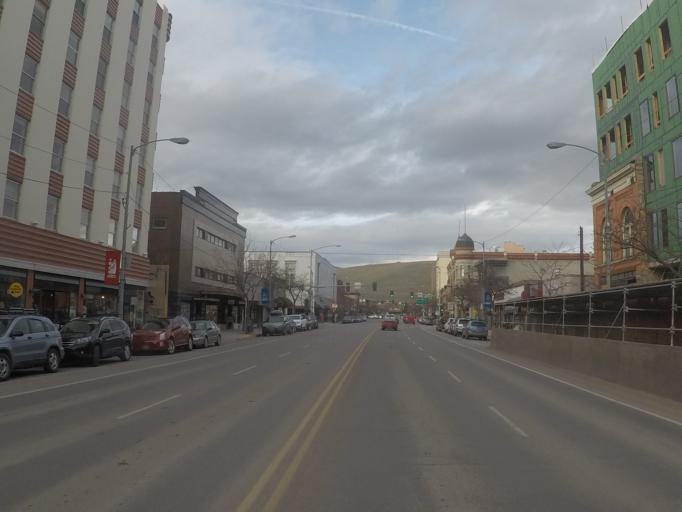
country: US
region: Montana
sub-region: Missoula County
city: Missoula
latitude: 46.8703
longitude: -113.9952
